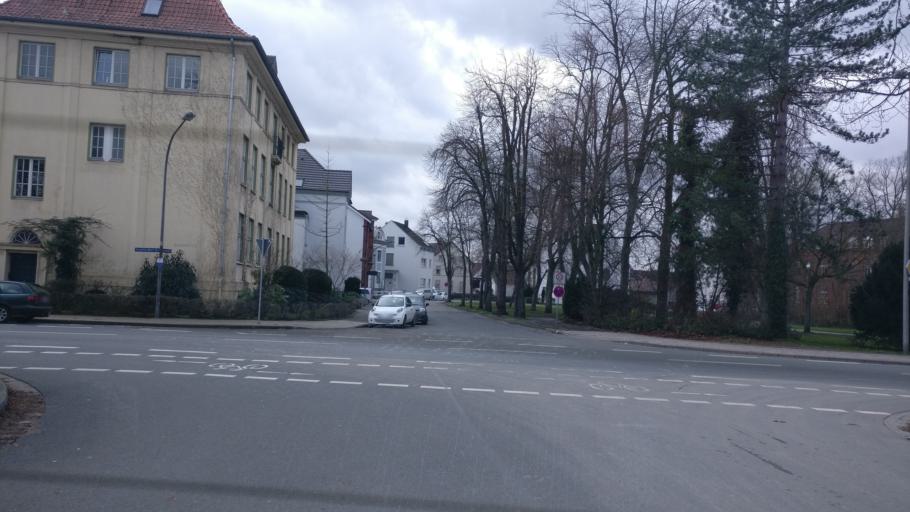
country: DE
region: North Rhine-Westphalia
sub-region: Regierungsbezirk Detmold
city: Lage
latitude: 51.9910
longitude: 8.8009
